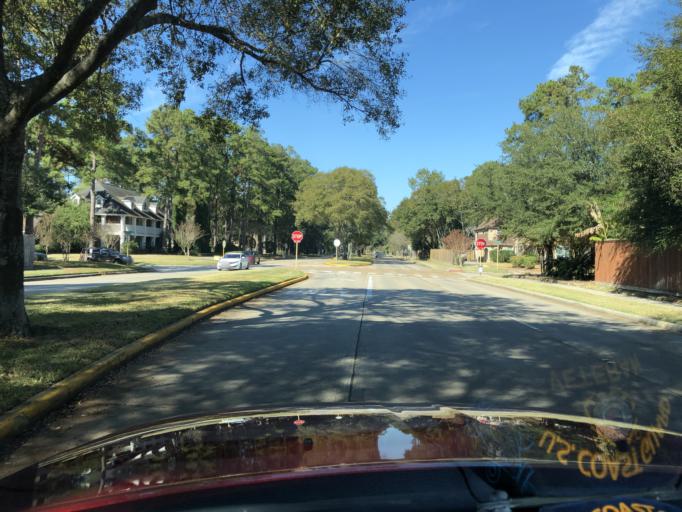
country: US
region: Texas
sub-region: Harris County
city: Tomball
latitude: 30.0215
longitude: -95.5471
